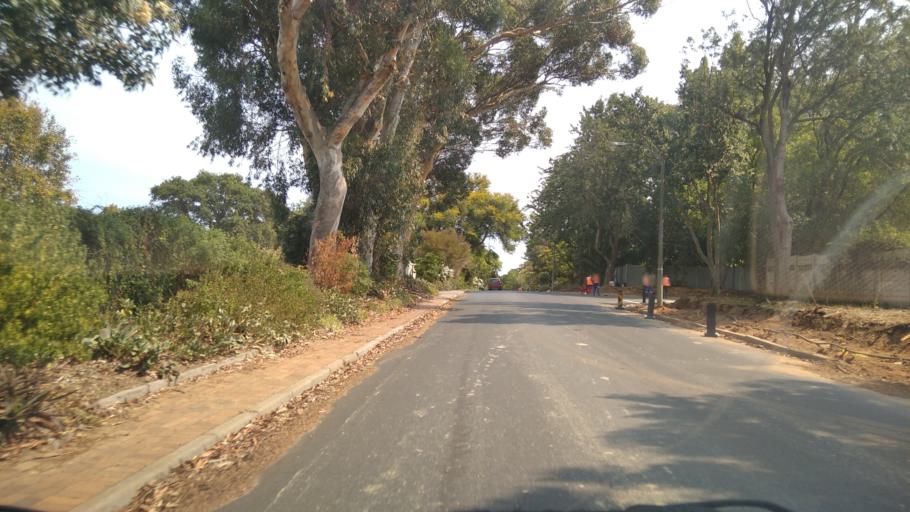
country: ZA
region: Western Cape
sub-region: City of Cape Town
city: Kraaifontein
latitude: -33.8190
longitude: 18.6576
